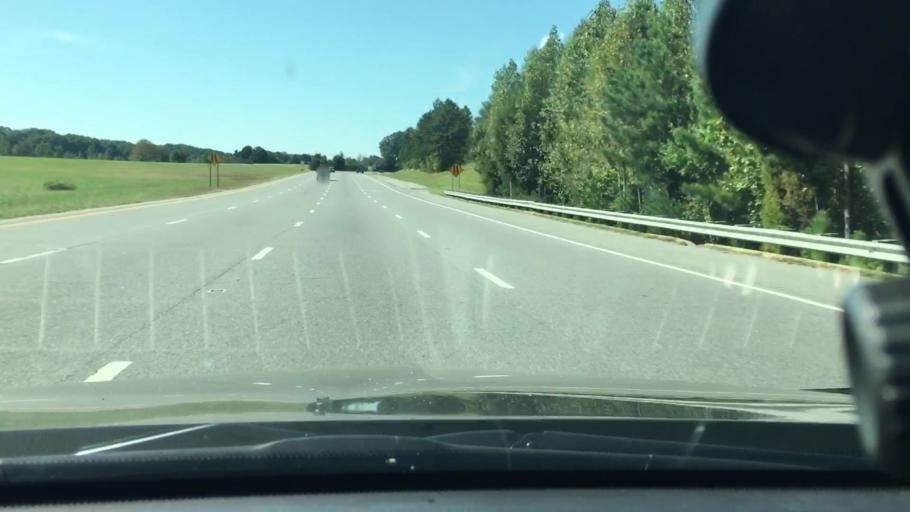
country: US
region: North Carolina
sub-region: Cleveland County
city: Kings Mountain
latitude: 35.2486
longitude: -81.3042
